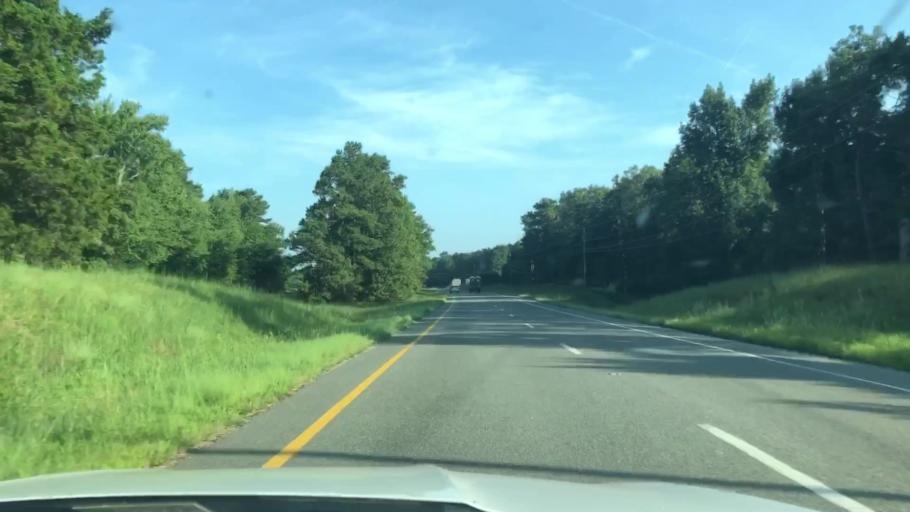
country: US
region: Virginia
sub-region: King and Queen County
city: King and Queen Court House
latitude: 37.7523
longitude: -76.7212
